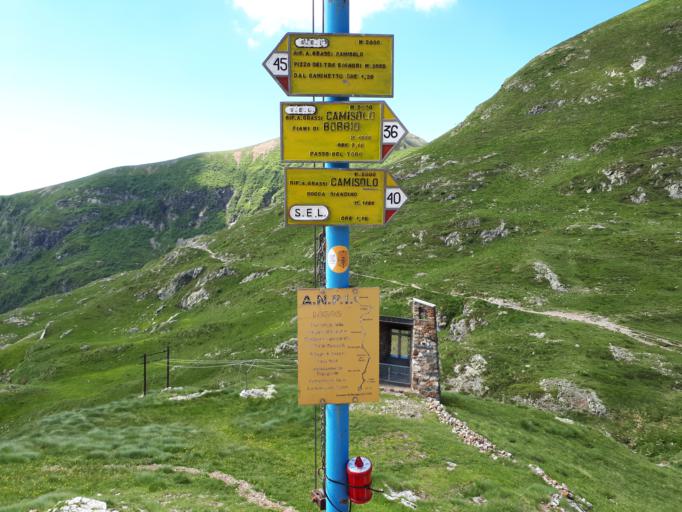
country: IT
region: Lombardy
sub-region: Provincia di Bergamo
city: Valtorta
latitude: 46.0093
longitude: 9.4918
